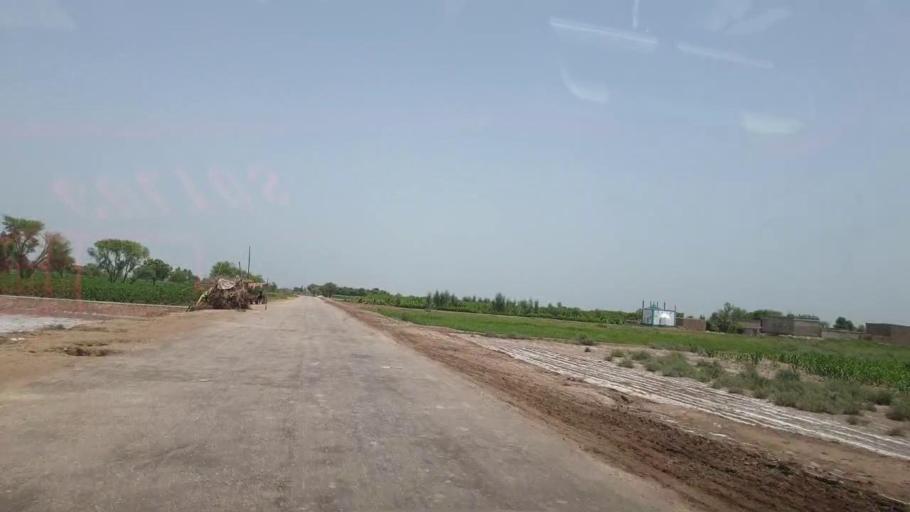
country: PK
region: Sindh
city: Daulatpur
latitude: 26.3894
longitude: 68.0912
